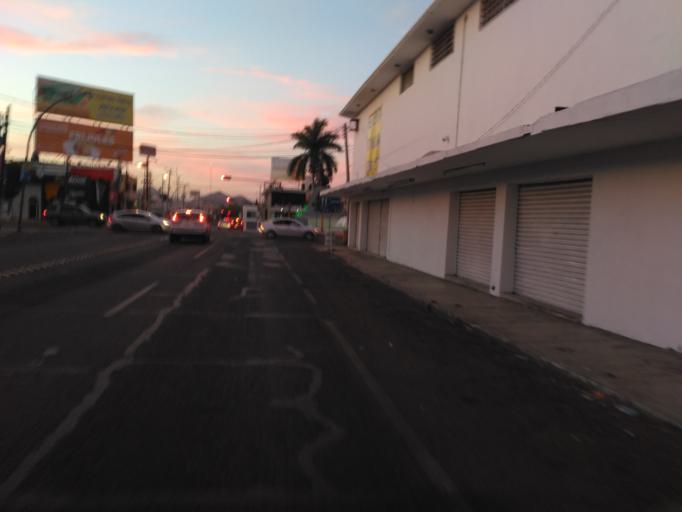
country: MX
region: Sinaloa
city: Culiacan
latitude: 24.8040
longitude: -107.4029
